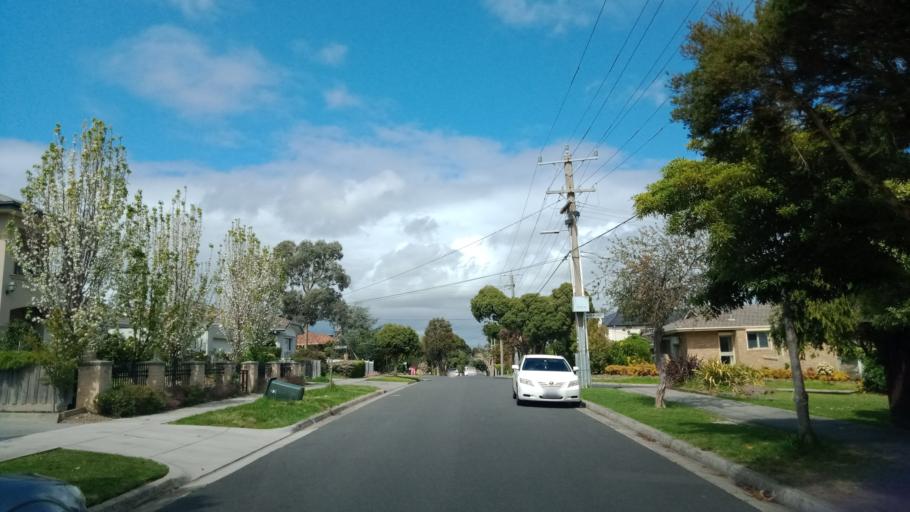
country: AU
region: Victoria
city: Burwood East
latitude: -37.8672
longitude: 145.1537
